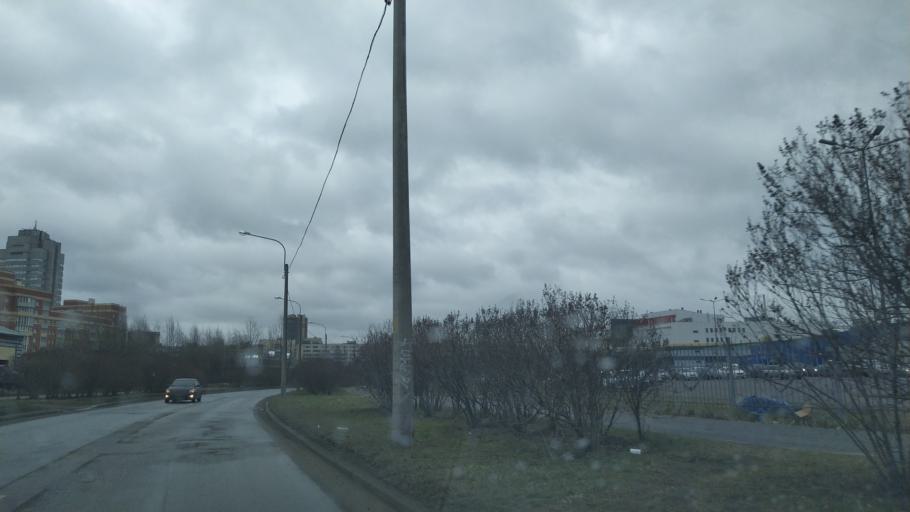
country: RU
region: St.-Petersburg
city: Komendantsky aerodrom
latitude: 60.0039
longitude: 30.2662
